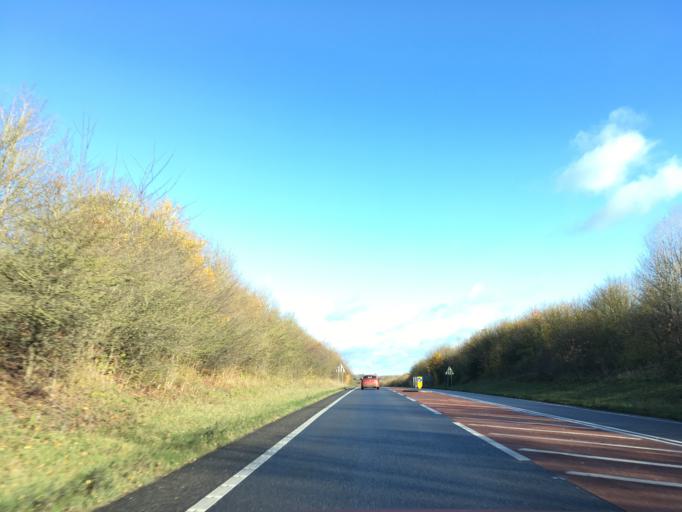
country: GB
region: England
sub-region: Worcestershire
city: Evesham
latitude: 52.0459
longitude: -1.9762
